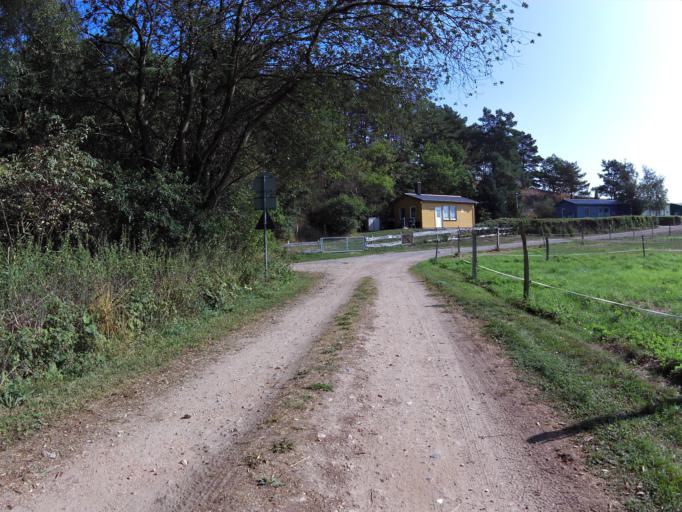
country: DE
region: Mecklenburg-Vorpommern
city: Loddin
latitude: 53.9647
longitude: 14.0445
